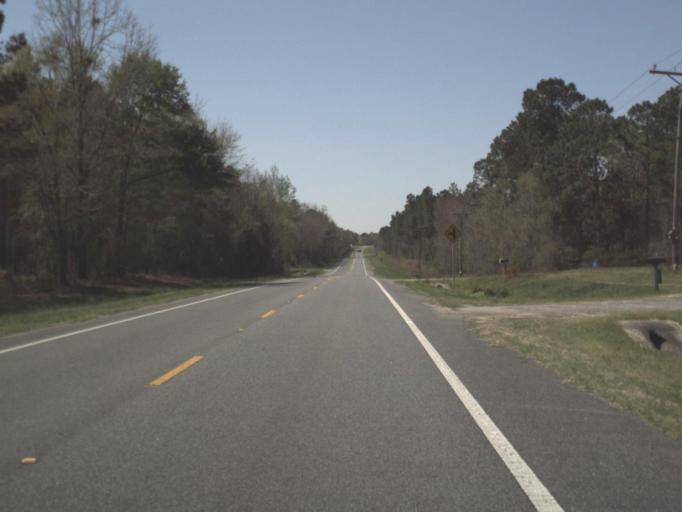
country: US
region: Alabama
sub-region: Geneva County
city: Geneva
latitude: 30.9563
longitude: -85.9059
